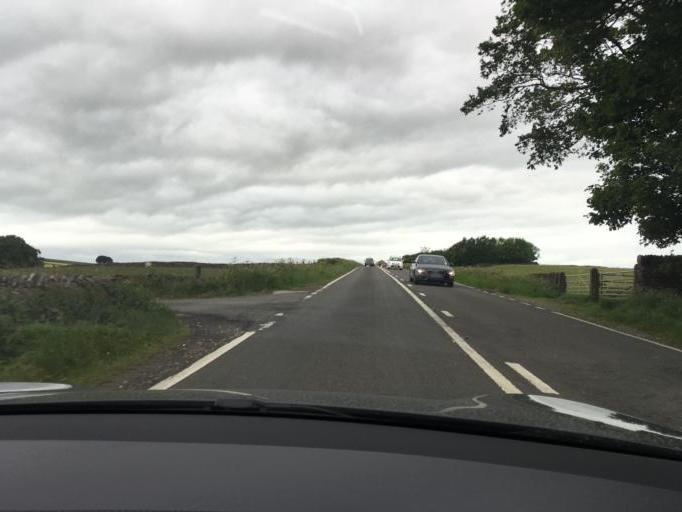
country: GB
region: England
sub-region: Derbyshire
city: Tideswell
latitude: 53.2871
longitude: -1.7749
